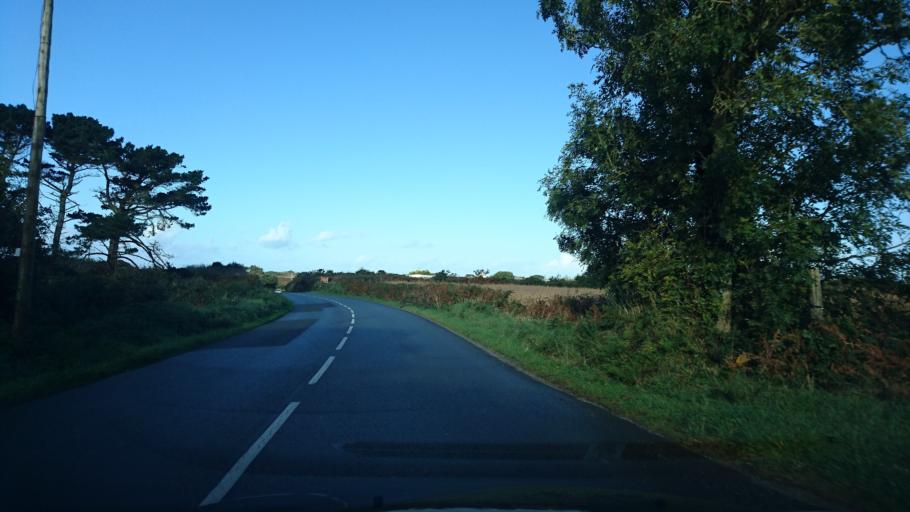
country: FR
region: Brittany
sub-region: Departement du Finistere
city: Plouarzel
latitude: 48.4416
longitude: -4.7446
